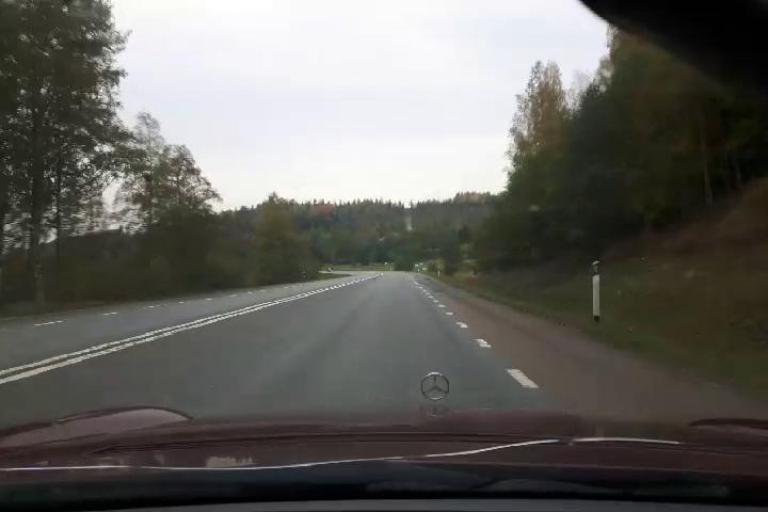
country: SE
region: Vaesternorrland
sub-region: Kramfors Kommun
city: Nordingra
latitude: 63.0071
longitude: 18.2684
